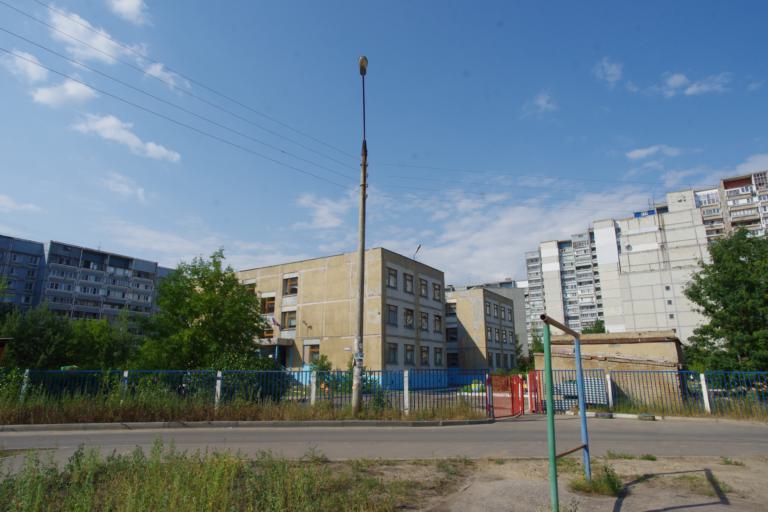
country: RU
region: Nizjnij Novgorod
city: Nizhniy Novgorod
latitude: 56.3435
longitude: 43.9401
